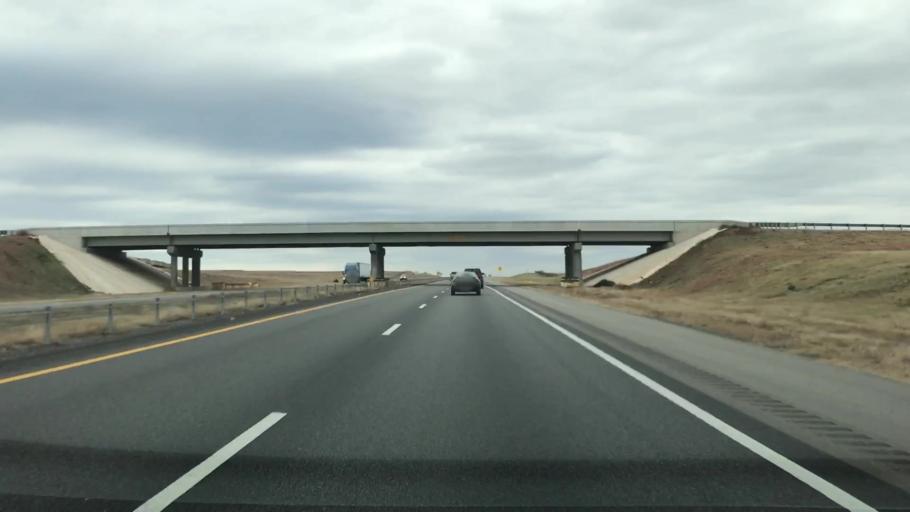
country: US
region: Oklahoma
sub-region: Beckham County
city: Elk City
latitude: 35.3859
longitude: -99.4692
